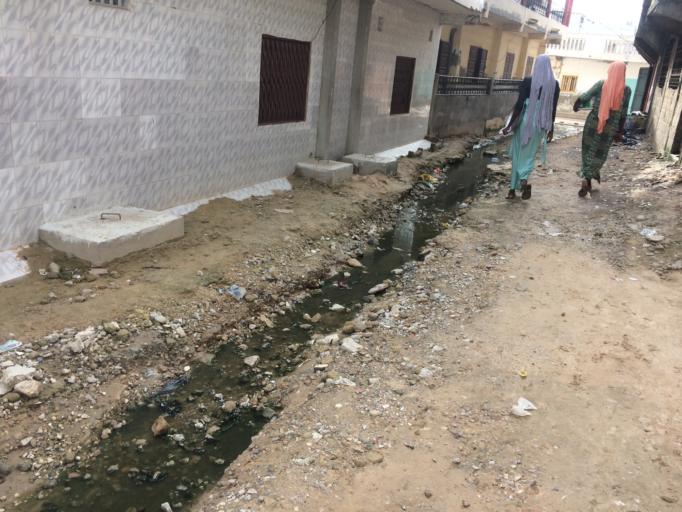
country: SN
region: Dakar
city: Pikine
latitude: 14.7445
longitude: -17.3223
